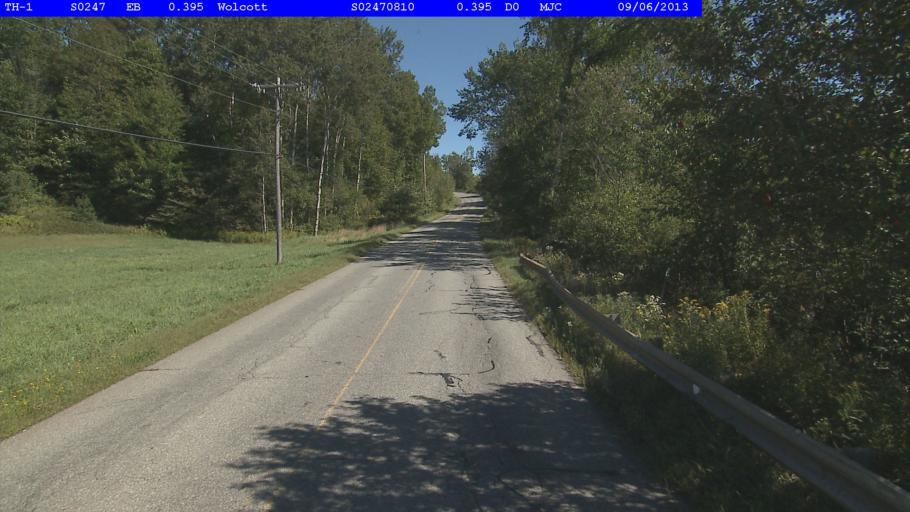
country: US
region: Vermont
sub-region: Lamoille County
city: Morrisville
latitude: 44.5641
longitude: -72.4872
